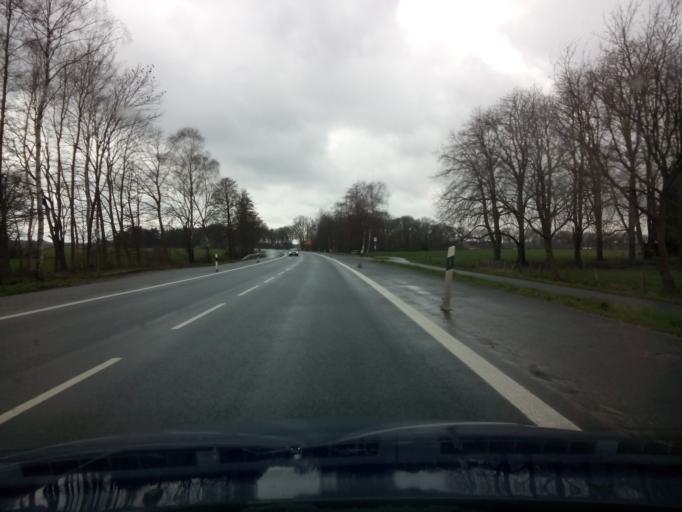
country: DE
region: Lower Saxony
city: Prinzhofte
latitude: 52.9639
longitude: 8.4990
